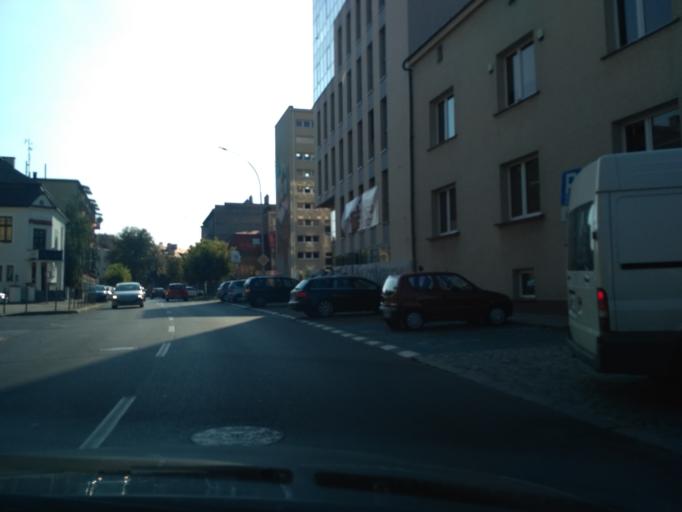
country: PL
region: Subcarpathian Voivodeship
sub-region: Rzeszow
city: Rzeszow
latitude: 50.0345
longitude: 21.9963
